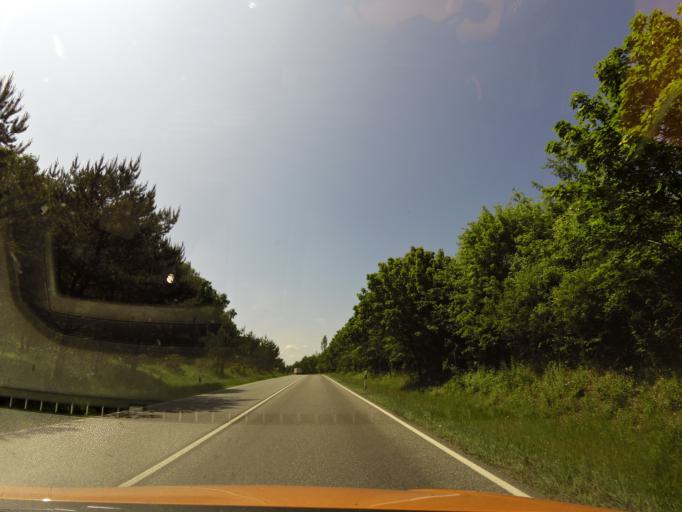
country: DE
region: Mecklenburg-Vorpommern
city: Selmsdorf
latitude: 53.8747
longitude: 10.7978
